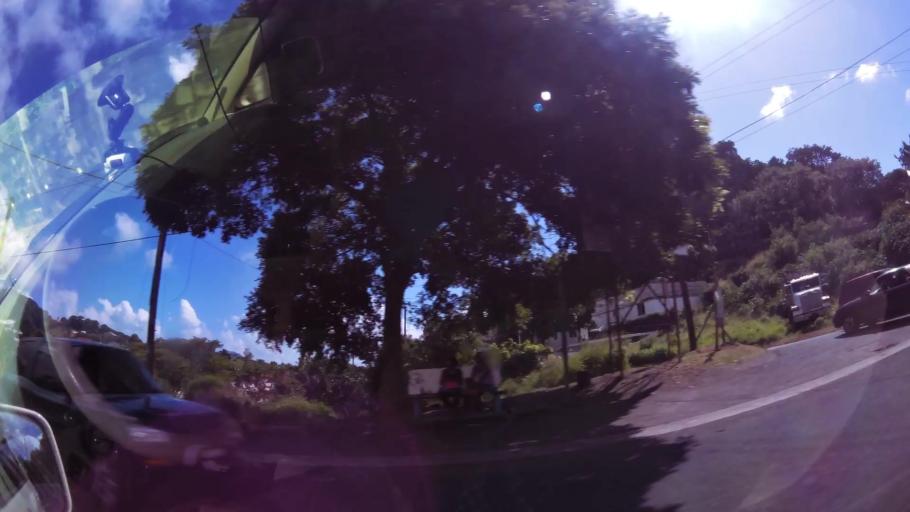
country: VC
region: Saint George
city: Kingstown
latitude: 13.1388
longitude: -61.2054
